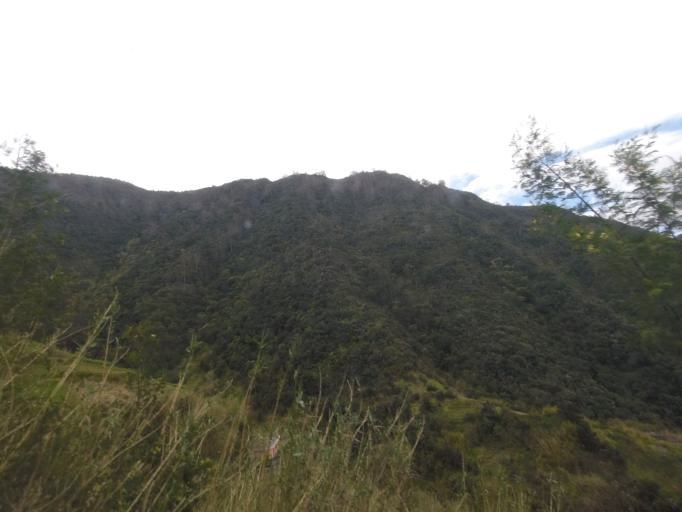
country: PT
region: Madeira
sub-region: Machico
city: Canical
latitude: 32.7631
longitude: -16.8091
